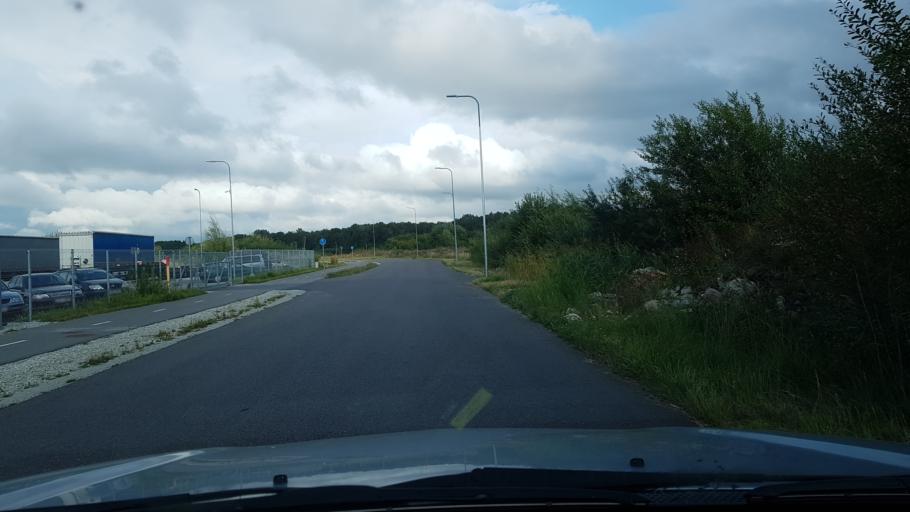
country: EE
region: Harju
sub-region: Rae vald
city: Jueri
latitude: 59.3804
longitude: 24.8490
